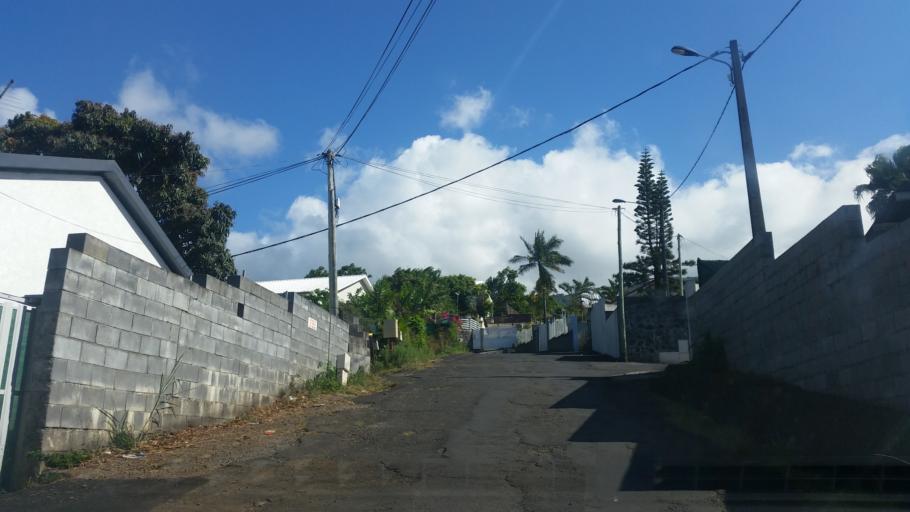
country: RE
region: Reunion
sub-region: Reunion
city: Sainte-Marie
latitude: -20.9331
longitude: 55.5314
